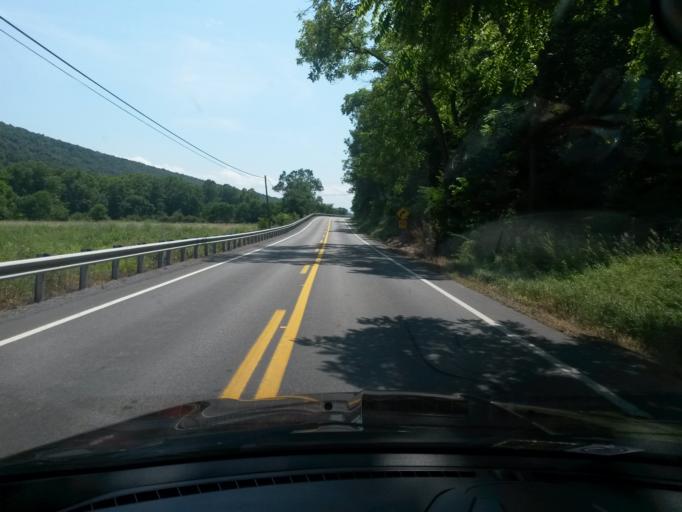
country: US
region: West Virginia
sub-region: Grant County
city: Petersburg
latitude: 39.0450
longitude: -79.1133
